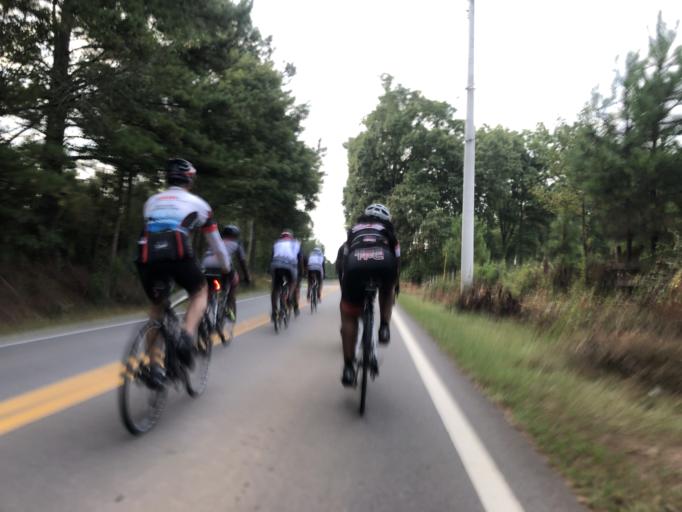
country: US
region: Georgia
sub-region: Fulton County
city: Palmetto
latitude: 33.6120
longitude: -84.6656
